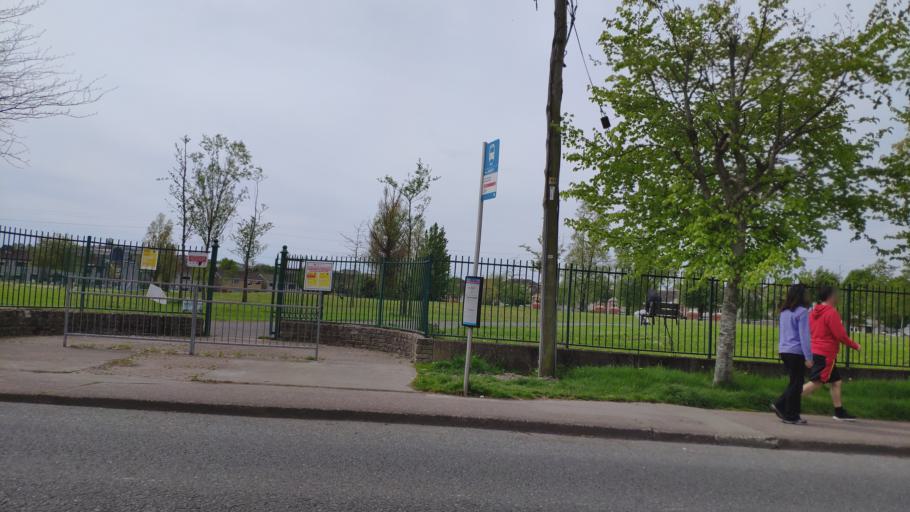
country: IE
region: Munster
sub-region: County Cork
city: Cork
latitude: 51.9203
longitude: -8.4541
